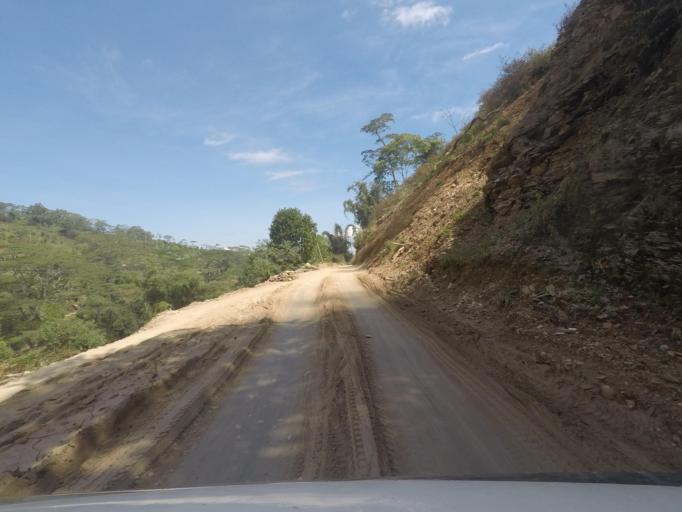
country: TL
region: Ermera
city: Gleno
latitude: -8.7522
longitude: 125.3318
